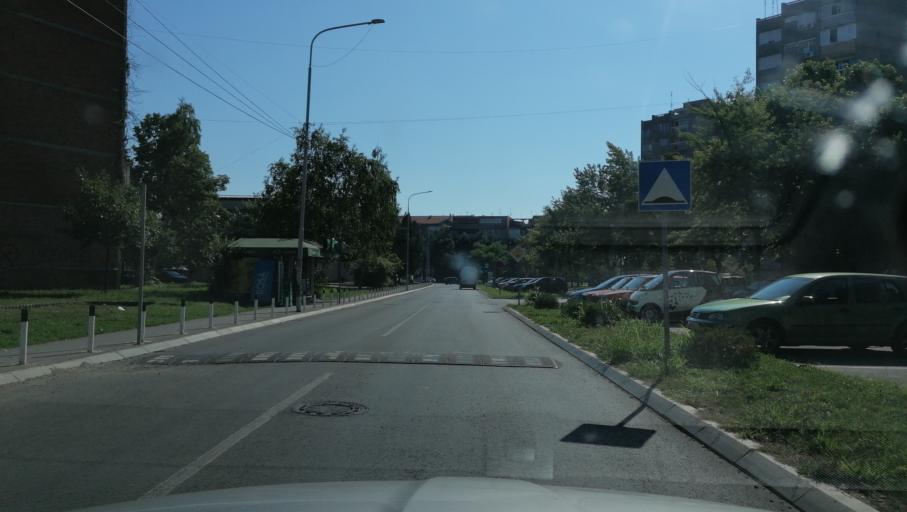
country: RS
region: Central Serbia
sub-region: Rasinski Okrug
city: Krusevac
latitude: 43.5673
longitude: 21.3303
